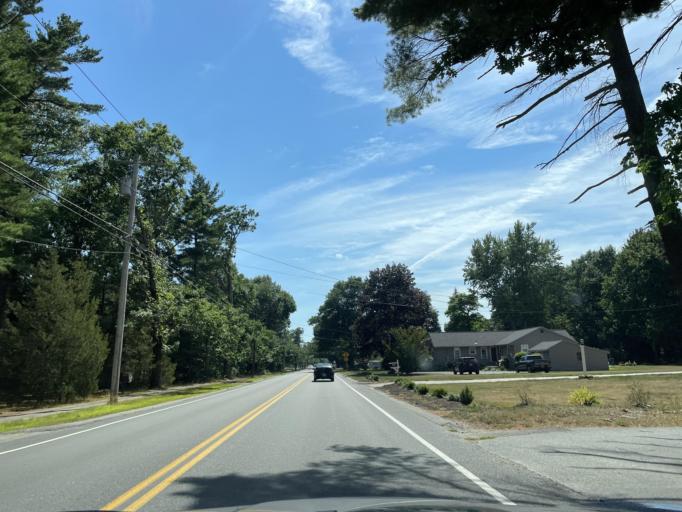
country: US
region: Massachusetts
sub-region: Norfolk County
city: Foxborough
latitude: 42.0762
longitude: -71.2359
